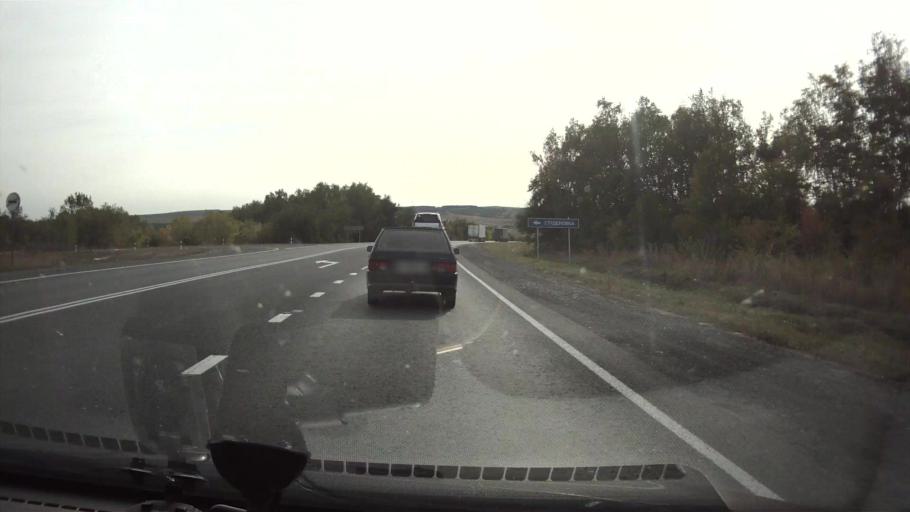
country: RU
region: Saratov
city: Sinodskoye
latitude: 51.9361
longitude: 46.5912
